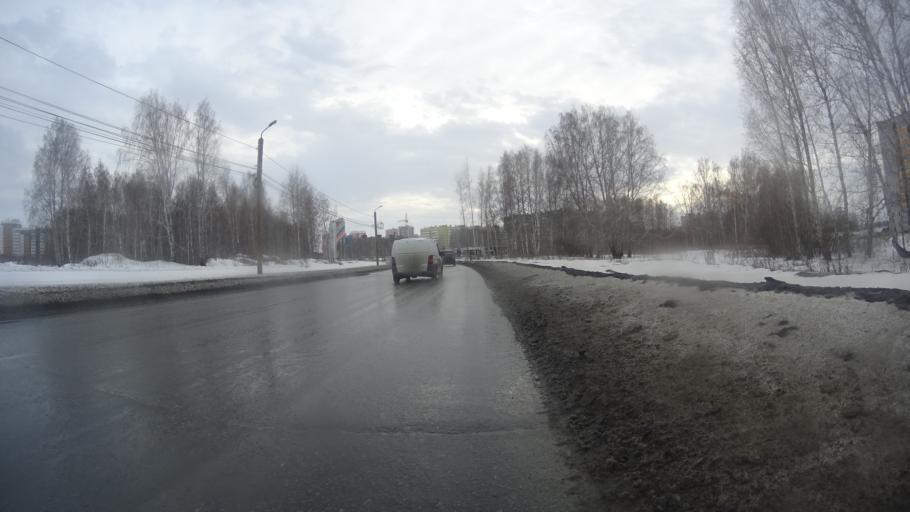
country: RU
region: Chelyabinsk
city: Roshchino
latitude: 55.2157
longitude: 61.2866
